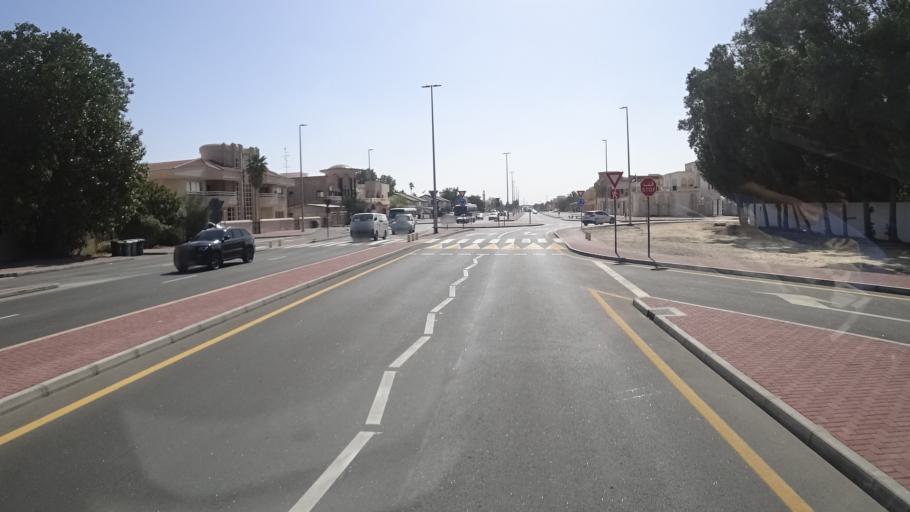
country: AE
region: Dubai
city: Dubai
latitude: 25.1587
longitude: 55.2099
